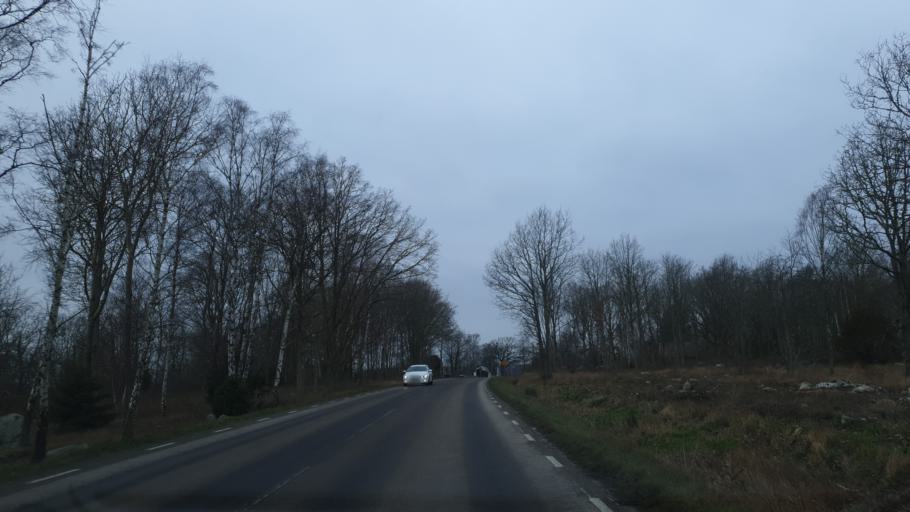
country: SE
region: Blekinge
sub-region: Karlskrona Kommun
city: Sturko
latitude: 56.1133
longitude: 15.6943
